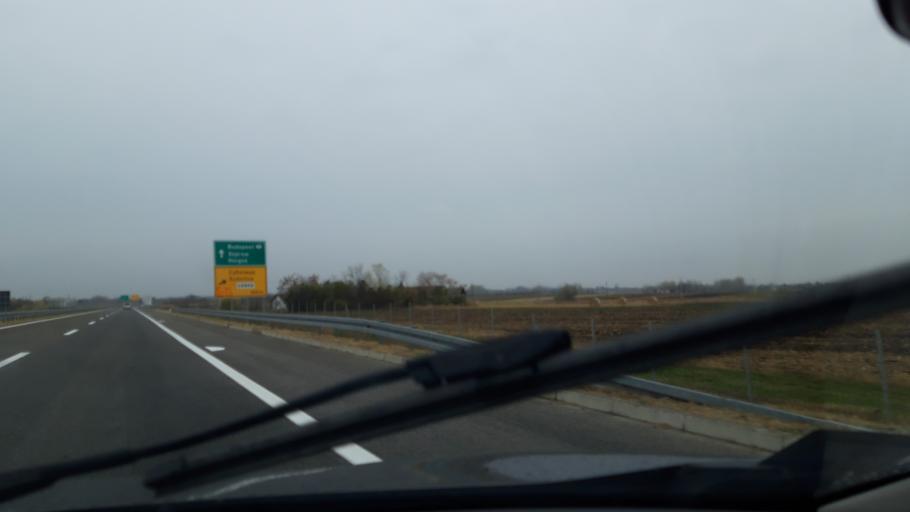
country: HU
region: Csongrad
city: Asotthalom
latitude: 46.0971
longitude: 19.7917
